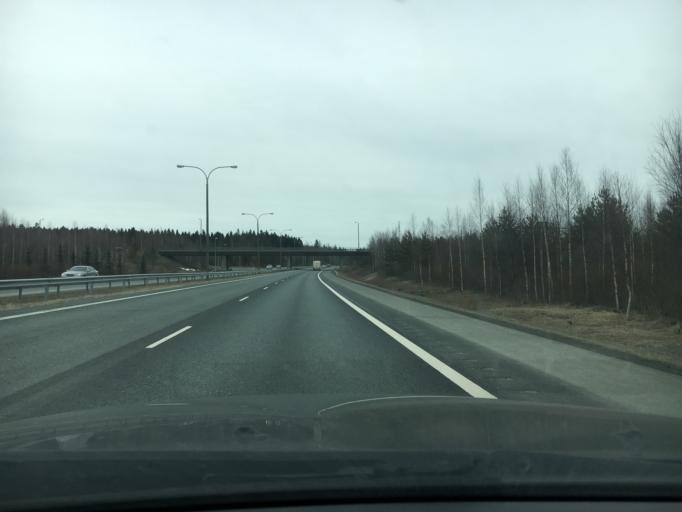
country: FI
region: Northern Savo
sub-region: Kuopio
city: Kuopio
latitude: 62.7974
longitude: 27.5948
